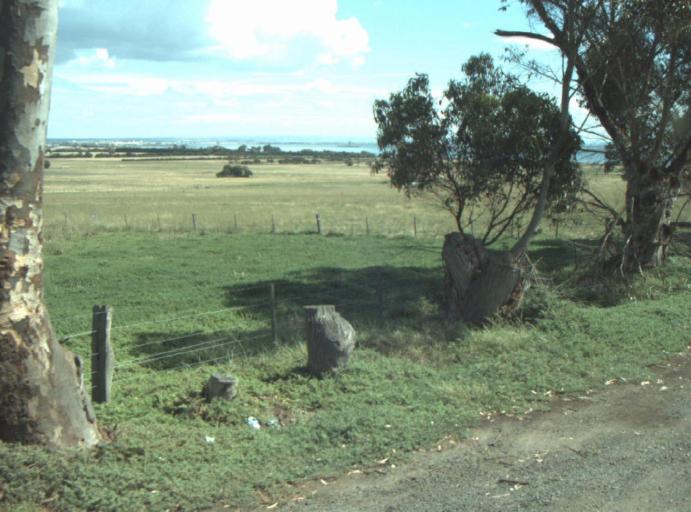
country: AU
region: Victoria
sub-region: Greater Geelong
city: Leopold
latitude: -38.1753
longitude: 144.4710
